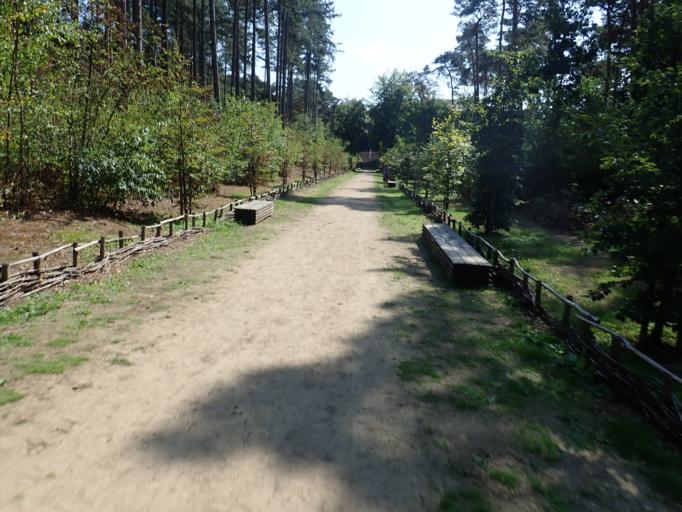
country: BE
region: Flanders
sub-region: Provincie Vlaams-Brabant
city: Scherpenheuvel-Zichem
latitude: 51.0310
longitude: 4.9818
